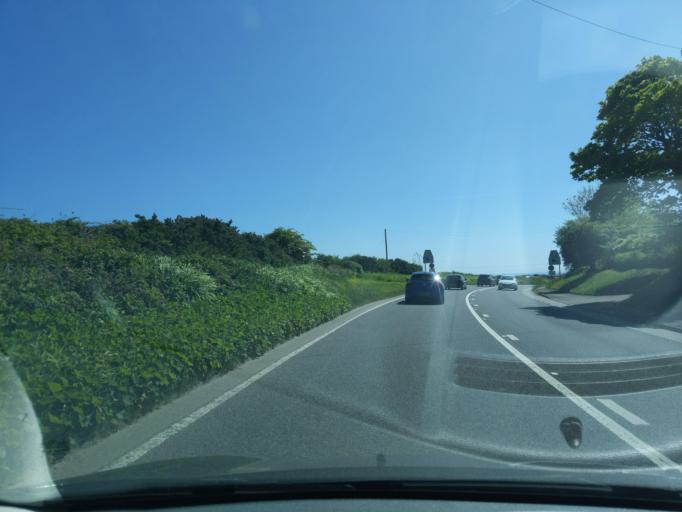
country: GB
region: England
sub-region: Cornwall
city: Wendron
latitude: 50.1585
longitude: -5.1863
